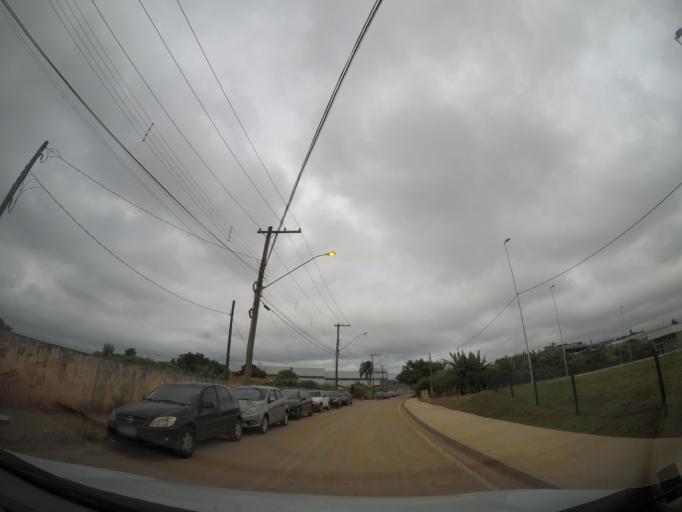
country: BR
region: Sao Paulo
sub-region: Aruja
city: Aruja
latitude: -23.4099
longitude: -46.3633
